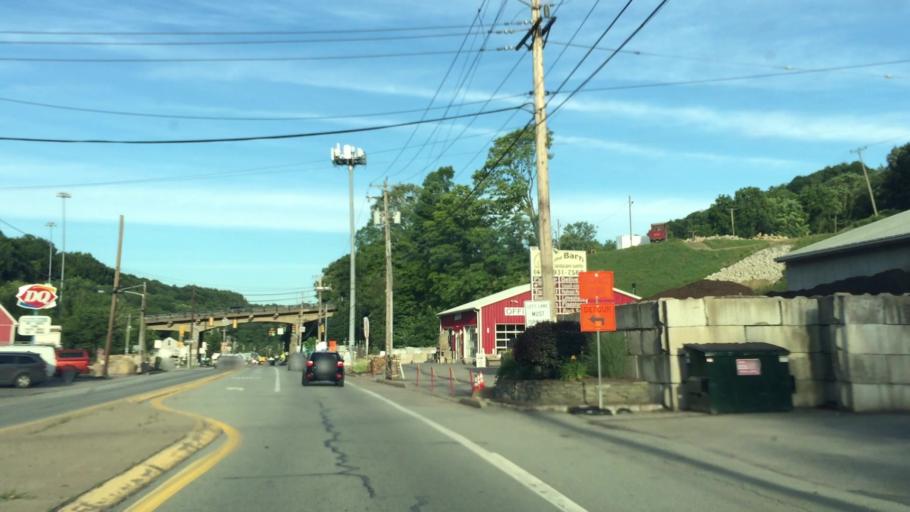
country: US
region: Pennsylvania
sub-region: Allegheny County
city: West View
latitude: 40.5144
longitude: -80.0066
